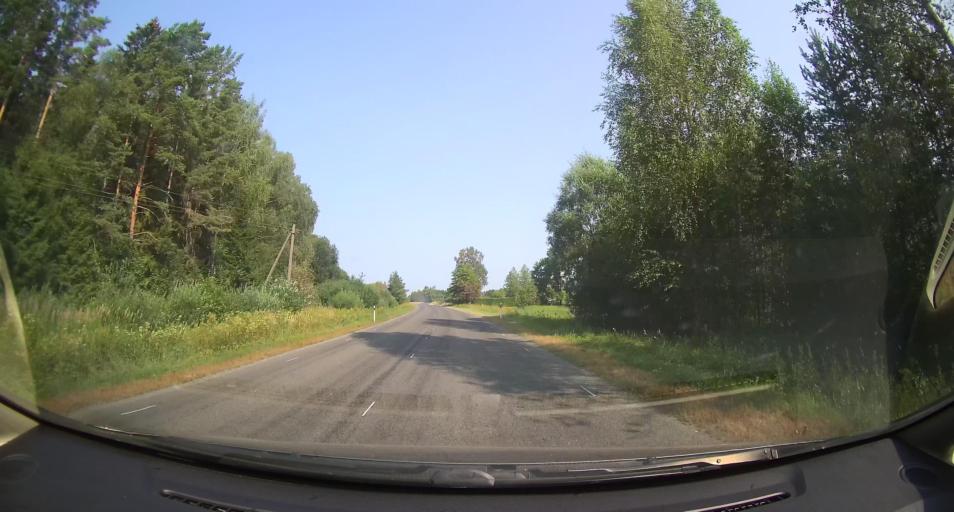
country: EE
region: Paernumaa
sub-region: Audru vald
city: Audru
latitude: 58.4302
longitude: 24.3150
